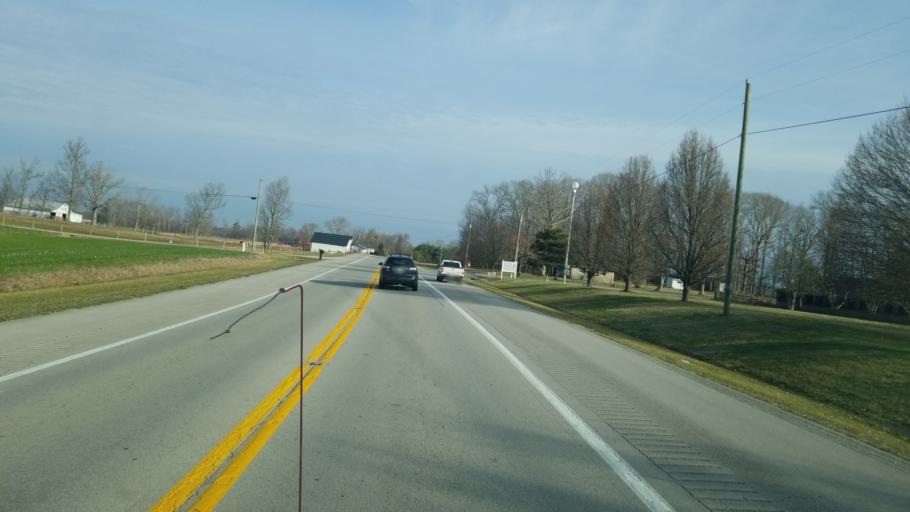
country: US
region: Kentucky
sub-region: Russell County
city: Russell Springs
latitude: 37.1413
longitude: -85.0317
